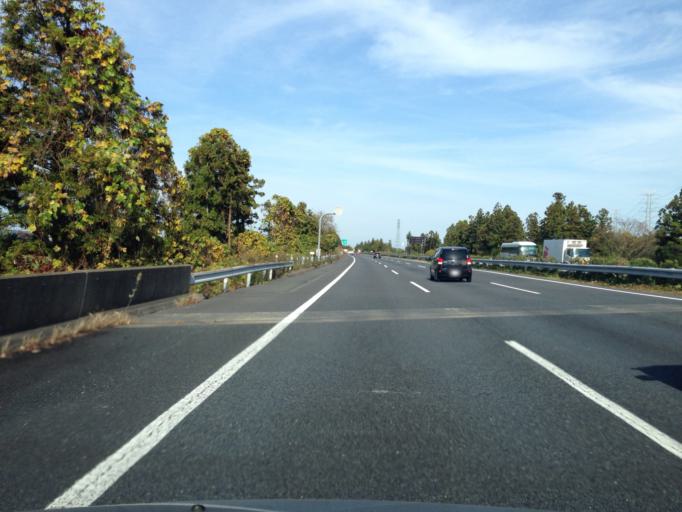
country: JP
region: Ibaraki
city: Mito-shi
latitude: 36.3692
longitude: 140.3822
